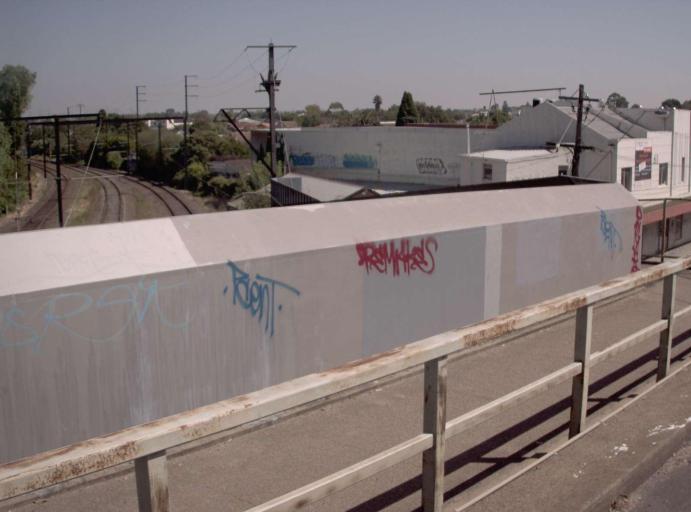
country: AU
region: Victoria
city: Hughesdale
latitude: -37.8994
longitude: 145.0871
